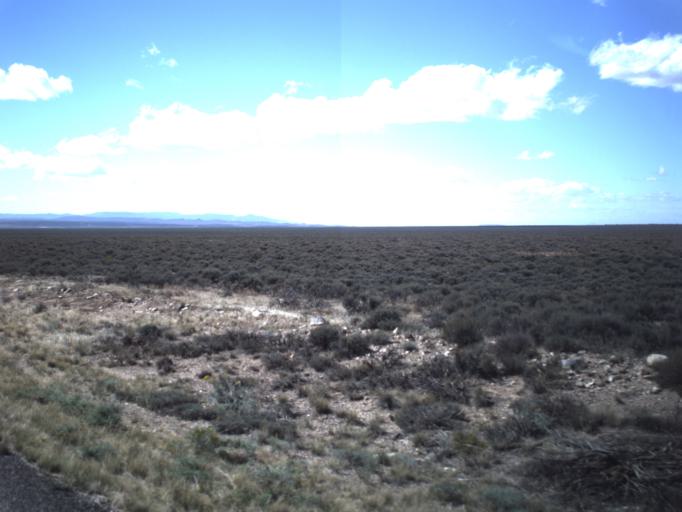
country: US
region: Utah
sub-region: Iron County
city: Enoch
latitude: 37.9525
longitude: -113.0141
